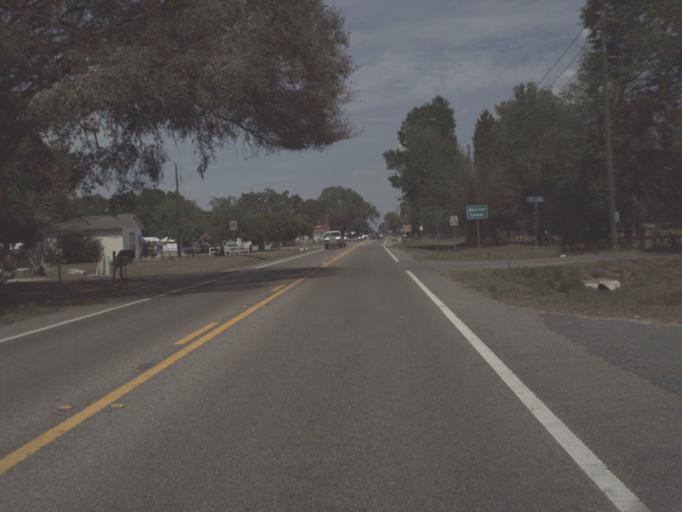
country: US
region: Florida
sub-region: Sumter County
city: Bushnell
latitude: 28.6461
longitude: -82.0548
